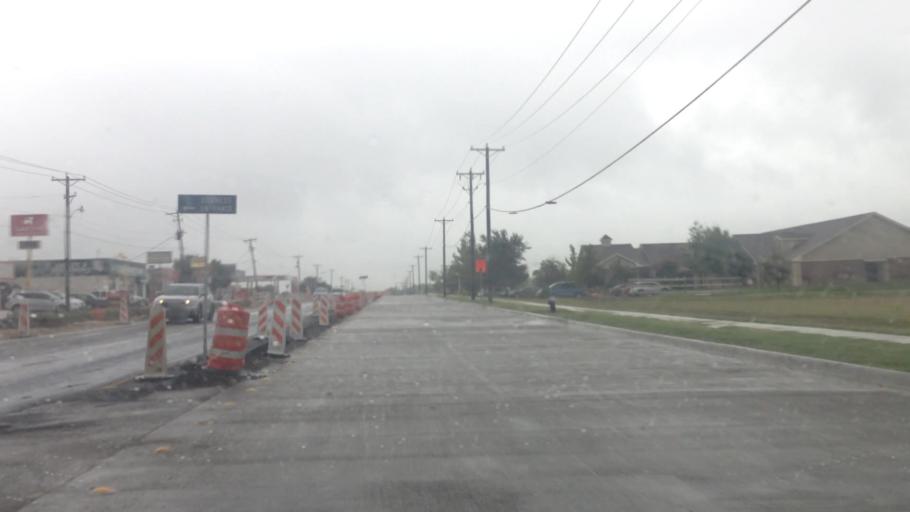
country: US
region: Texas
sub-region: Tarrant County
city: Watauga
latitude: 32.8694
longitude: -97.2379
